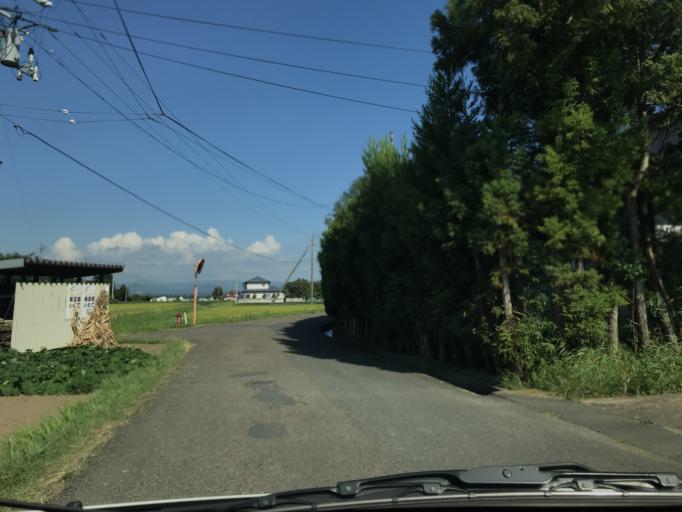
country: JP
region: Iwate
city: Mizusawa
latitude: 39.1601
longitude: 141.1260
